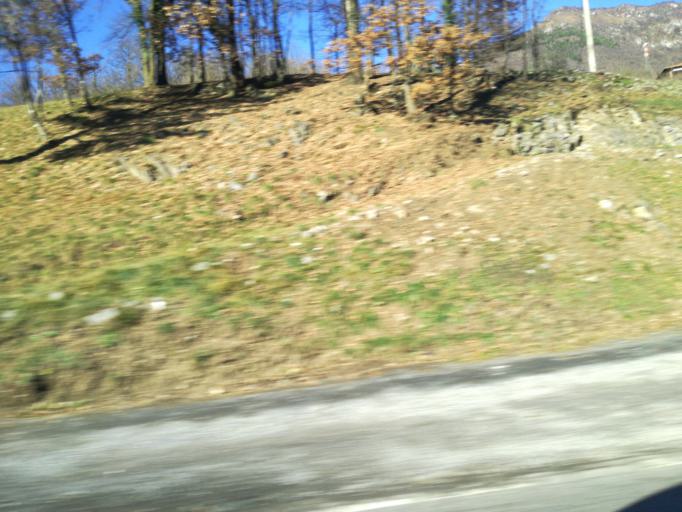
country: IT
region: Lombardy
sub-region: Provincia di Bergamo
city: Piangaiano
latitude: 45.7918
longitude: 10.0035
